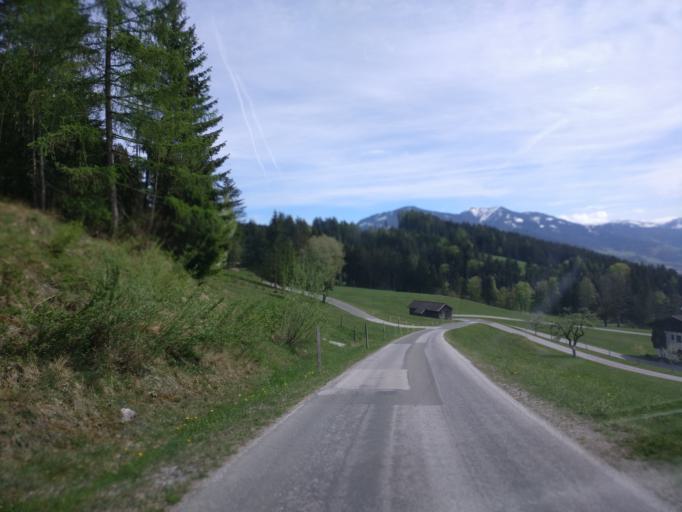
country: AT
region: Salzburg
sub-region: Politischer Bezirk Sankt Johann im Pongau
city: Pfarrwerfen
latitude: 47.4735
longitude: 13.2075
